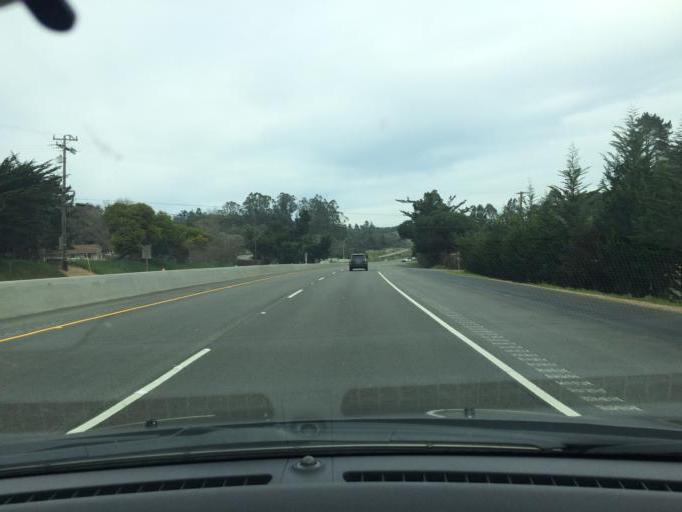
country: US
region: California
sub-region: Monterey County
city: Prunedale
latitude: 36.8129
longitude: -121.6420
